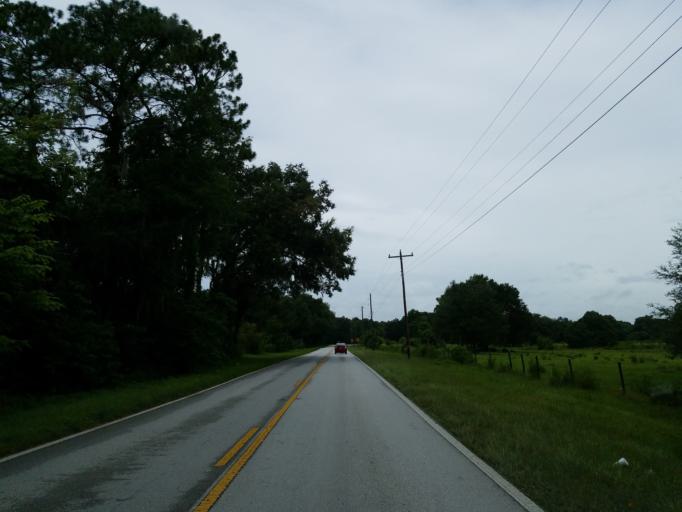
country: US
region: Florida
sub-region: Sumter County
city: Bushnell
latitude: 28.6690
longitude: -82.1810
